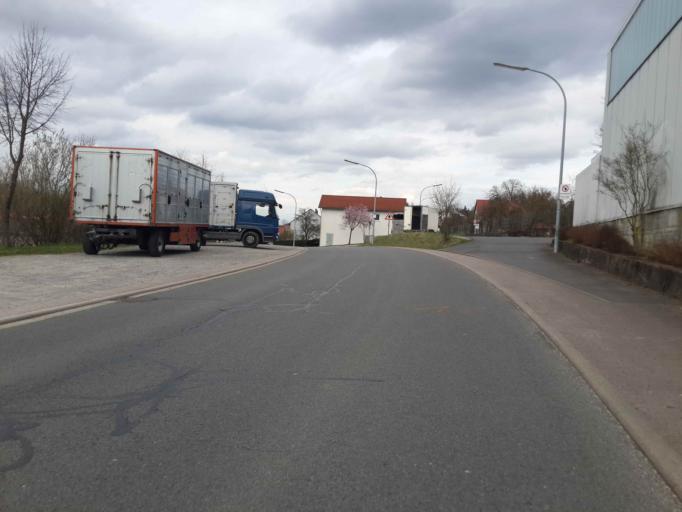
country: DE
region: Baden-Wuerttemberg
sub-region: Karlsruhe Region
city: Osterburken
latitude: 49.4256
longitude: 9.4206
